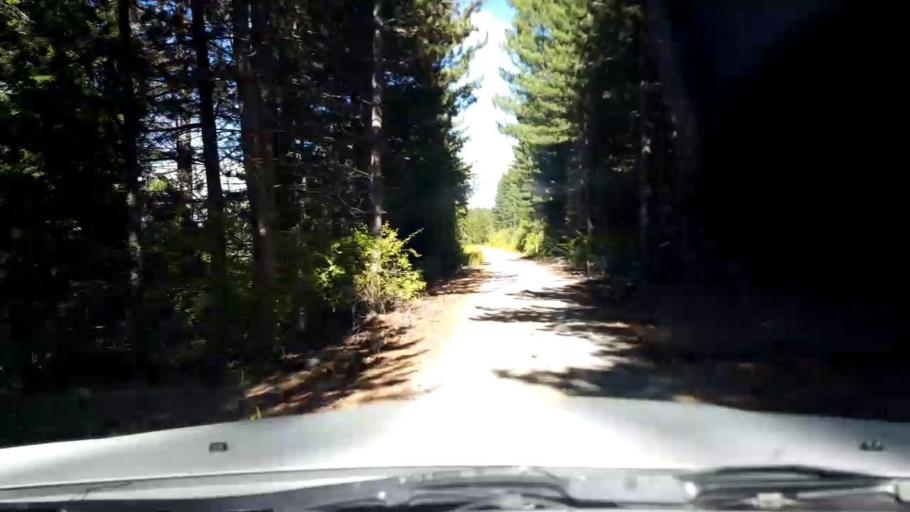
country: NZ
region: Canterbury
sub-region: Timaru District
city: Pleasant Point
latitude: -44.0129
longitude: 170.4665
